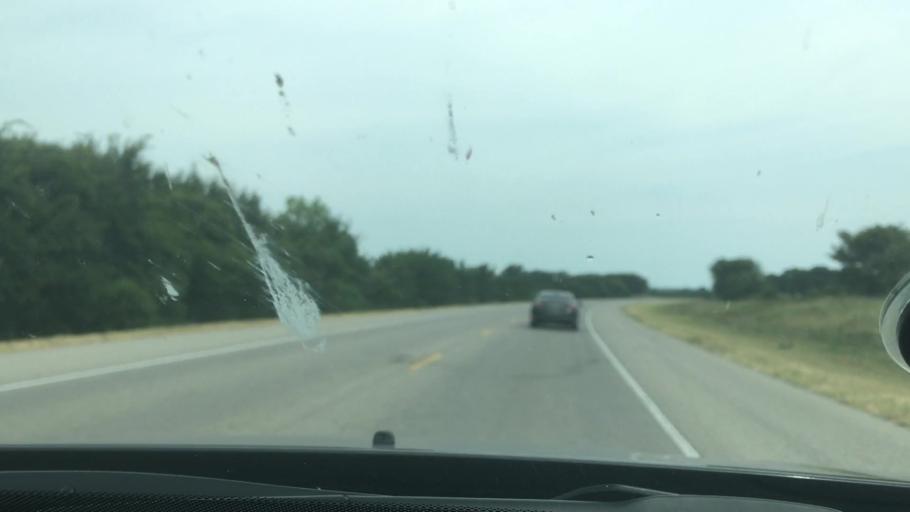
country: US
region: Oklahoma
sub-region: Pontotoc County
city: Ada
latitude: 34.6888
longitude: -96.5947
